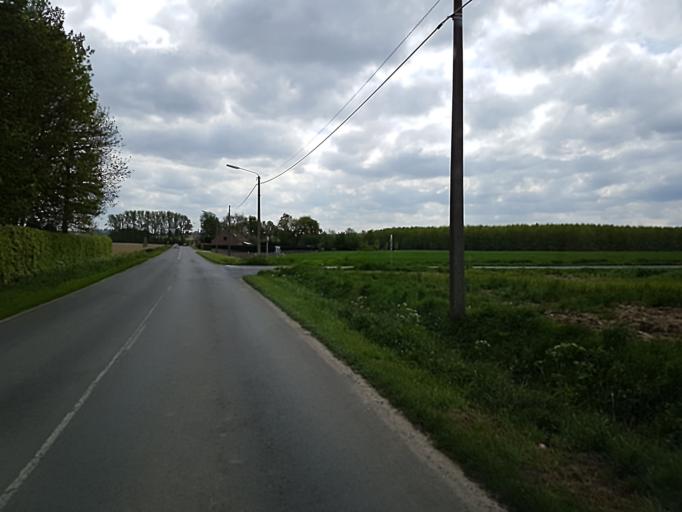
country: BE
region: Wallonia
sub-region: Province du Hainaut
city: Celles
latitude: 50.6953
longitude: 3.4711
